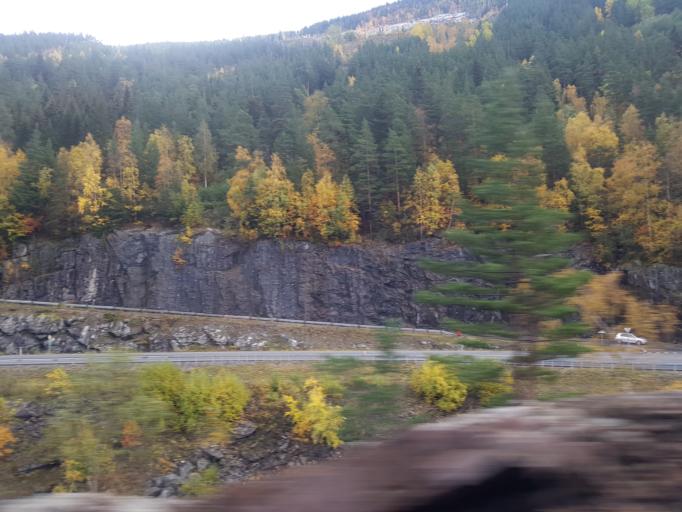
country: NO
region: Oppland
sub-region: Sel
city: Otta
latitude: 61.8784
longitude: 9.4078
